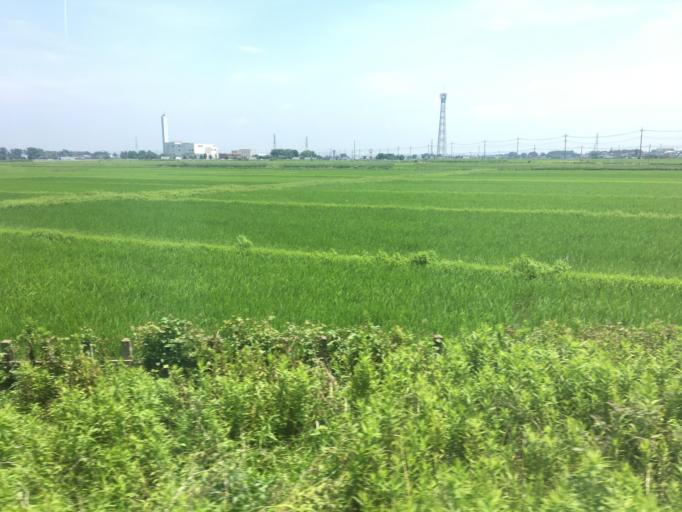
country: JP
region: Saitama
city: Menuma
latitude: 36.2633
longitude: 139.4224
